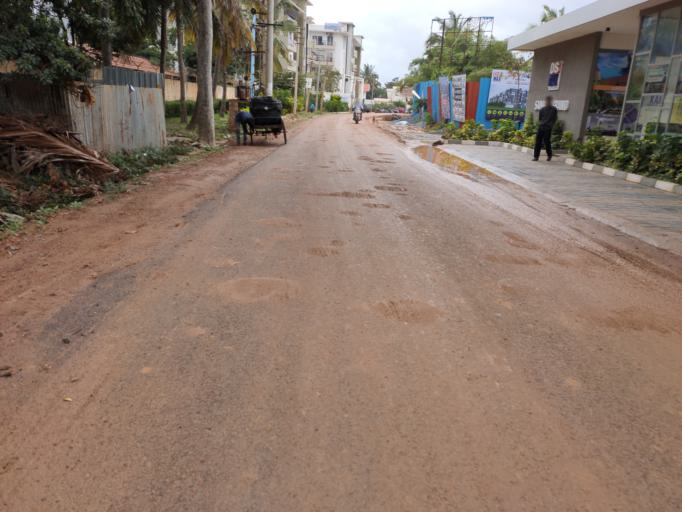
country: IN
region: Karnataka
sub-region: Bangalore Rural
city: Hoskote
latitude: 13.0071
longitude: 77.7627
